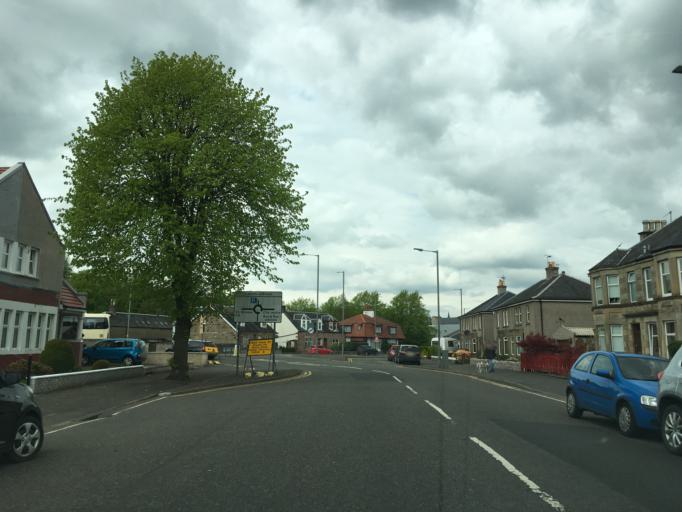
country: GB
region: Scotland
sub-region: Stirling
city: Stirling
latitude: 56.1120
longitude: -3.9317
